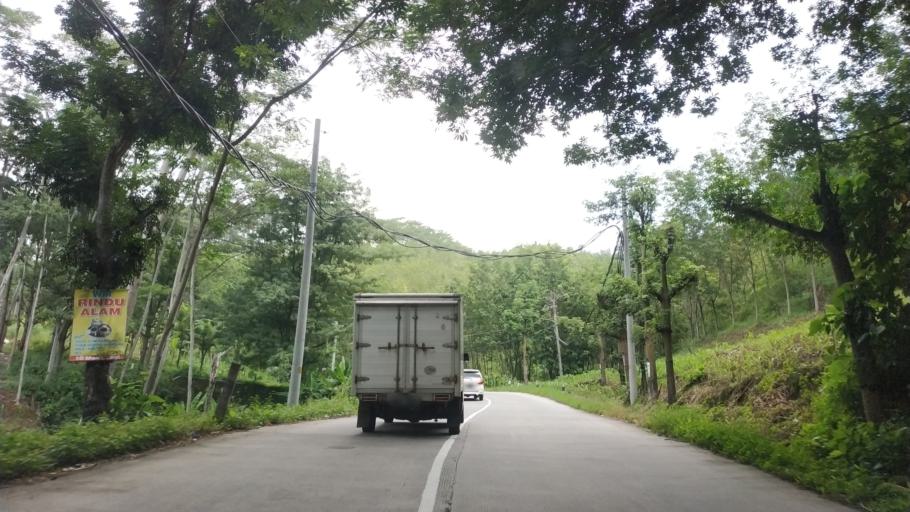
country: ID
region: Central Java
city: Weleri
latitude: -7.0030
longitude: 110.0601
